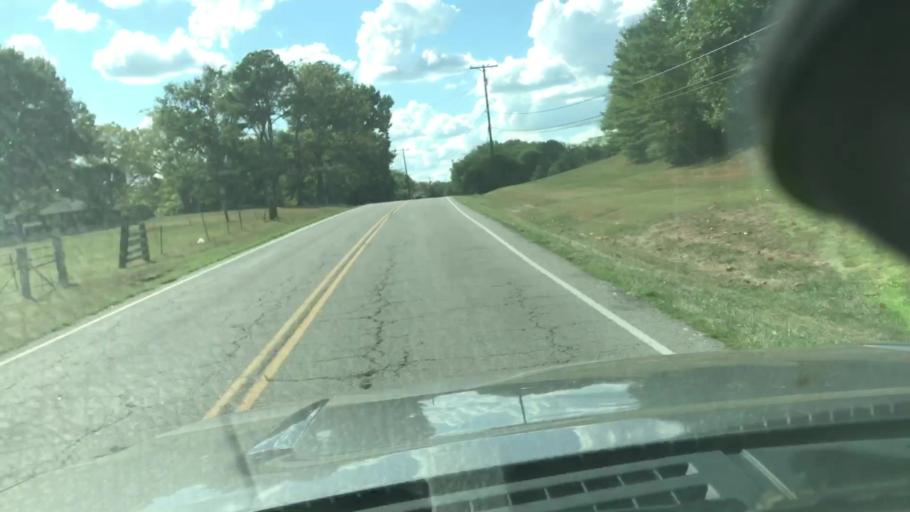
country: US
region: Tennessee
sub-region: Davidson County
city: Forest Hills
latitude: 36.0271
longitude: -86.9044
